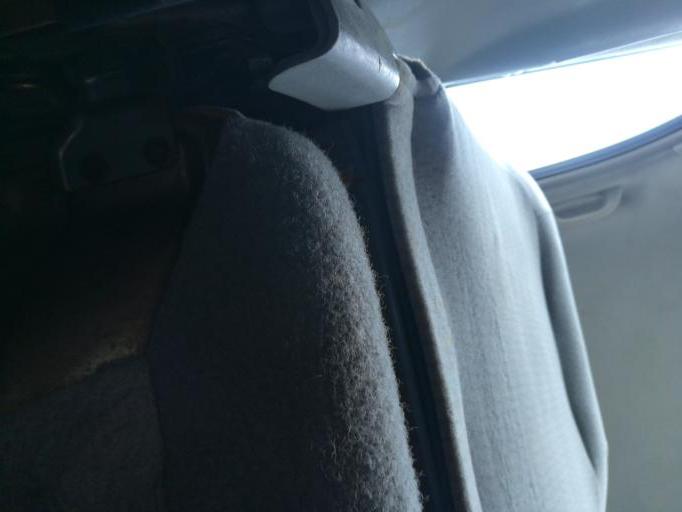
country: NG
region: Lagos
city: Lagos
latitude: 6.4478
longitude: 3.3931
